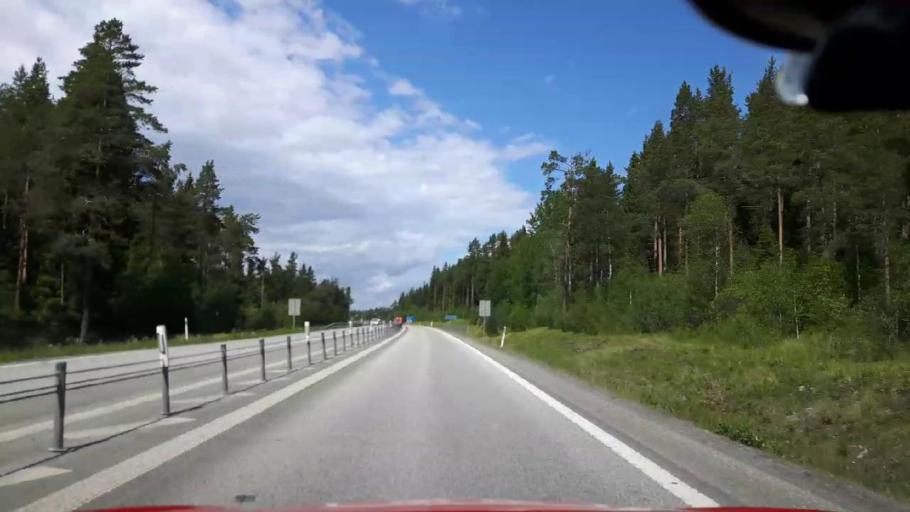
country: SE
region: Jaemtland
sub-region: OEstersunds Kommun
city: Ostersund
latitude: 63.1969
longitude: 14.6864
